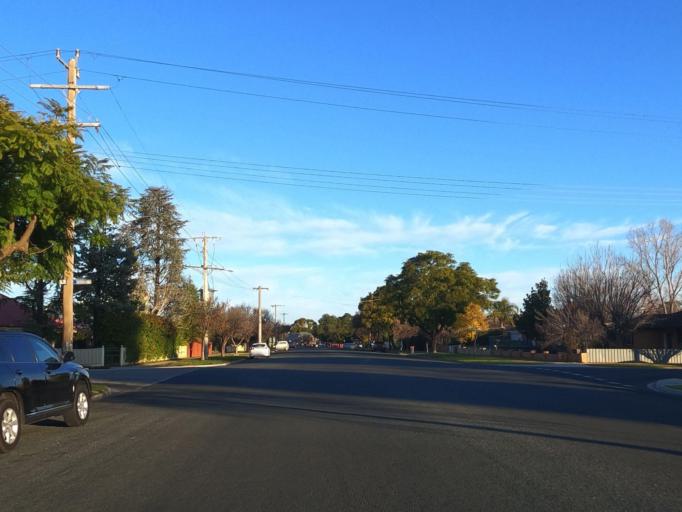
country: AU
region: Victoria
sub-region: Swan Hill
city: Swan Hill
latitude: -35.3462
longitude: 143.5601
